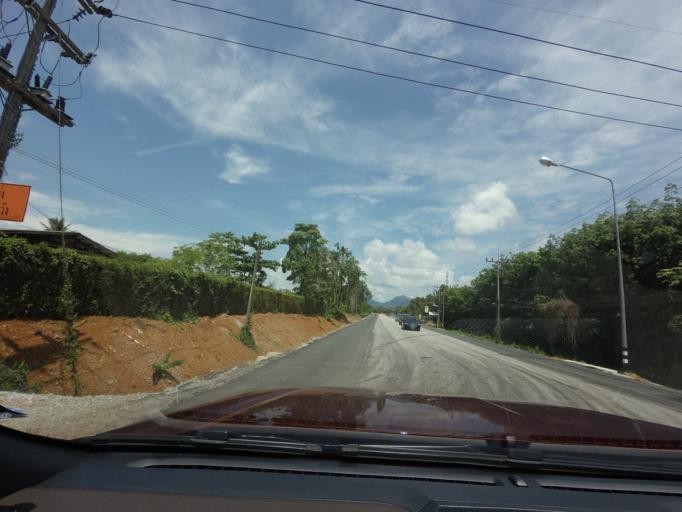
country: TH
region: Narathiwat
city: Ra-ngae
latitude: 6.2861
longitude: 101.7037
